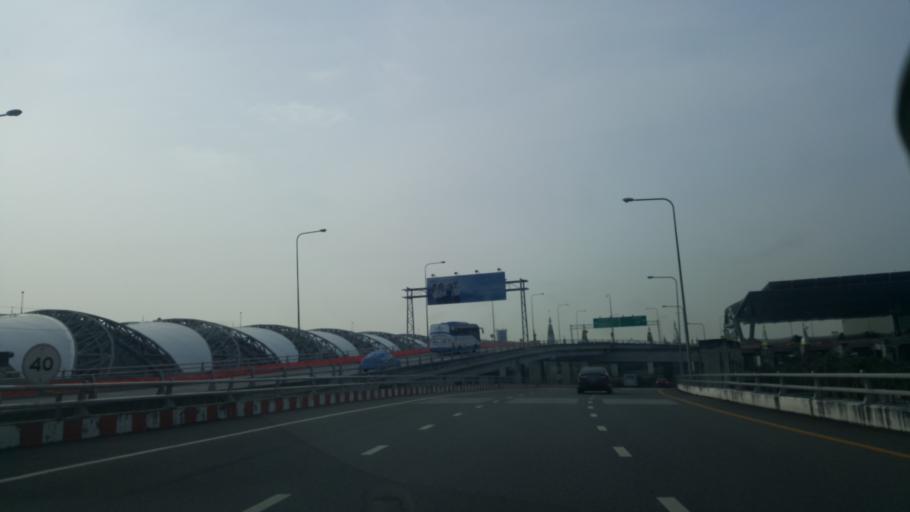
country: TH
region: Bangkok
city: Lat Krabang
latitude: 13.6953
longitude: 100.7544
